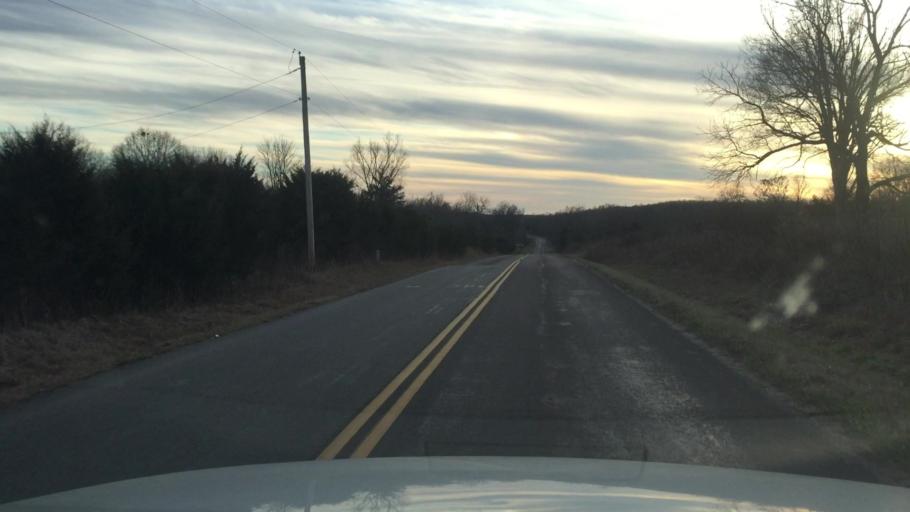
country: US
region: Missouri
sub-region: Miller County
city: Eldon
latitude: 38.3680
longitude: -92.6814
